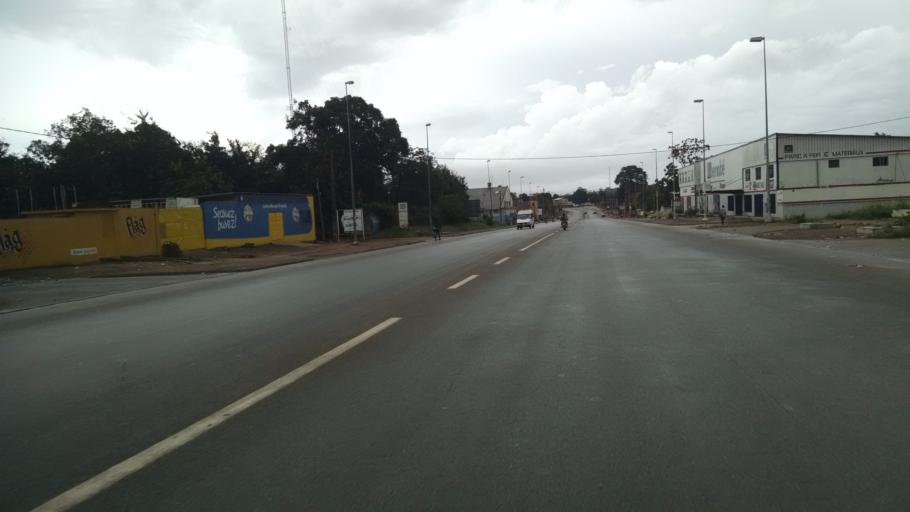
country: CI
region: Vallee du Bandama
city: Bouake
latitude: 7.6834
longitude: -5.0394
